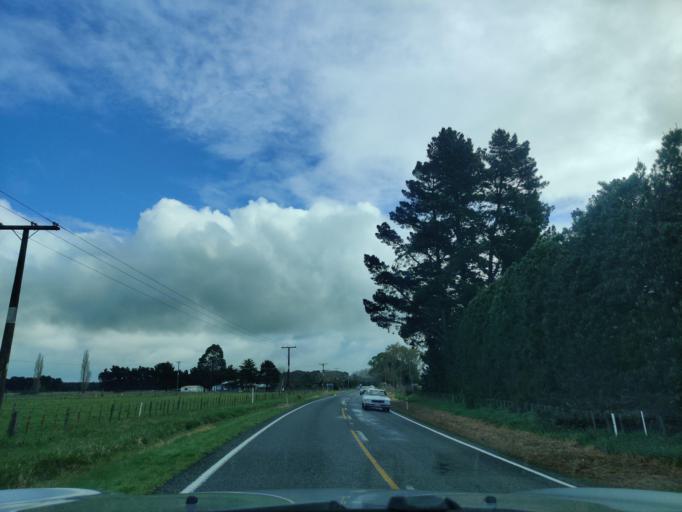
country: NZ
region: Hawke's Bay
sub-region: Hastings District
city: Hastings
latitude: -40.0210
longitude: 176.3362
